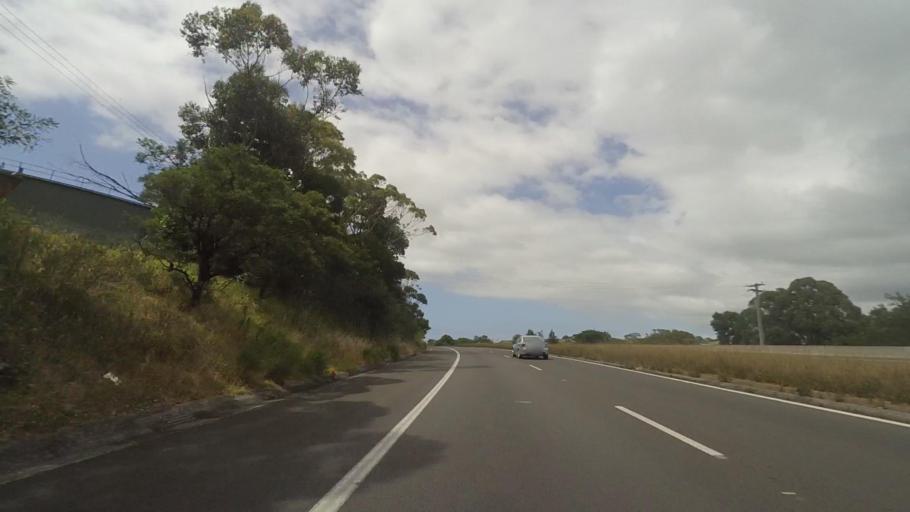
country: AU
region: New South Wales
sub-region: Kiama
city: Kiama
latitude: -34.6729
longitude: 150.8429
